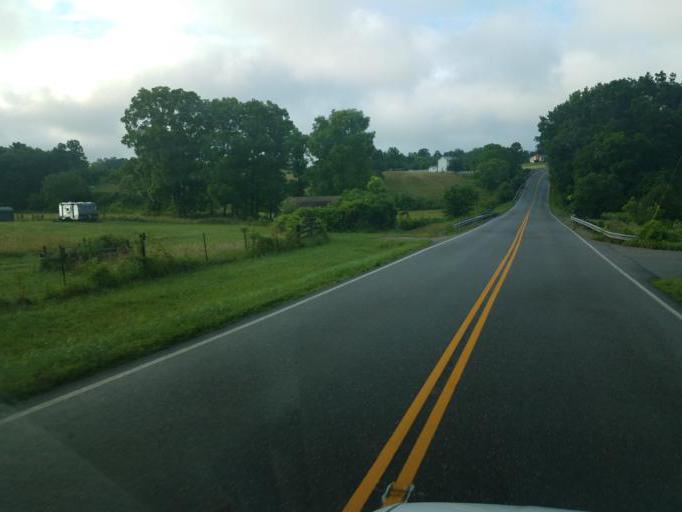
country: US
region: Ohio
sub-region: Jackson County
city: Oak Hill
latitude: 38.8073
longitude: -82.3997
